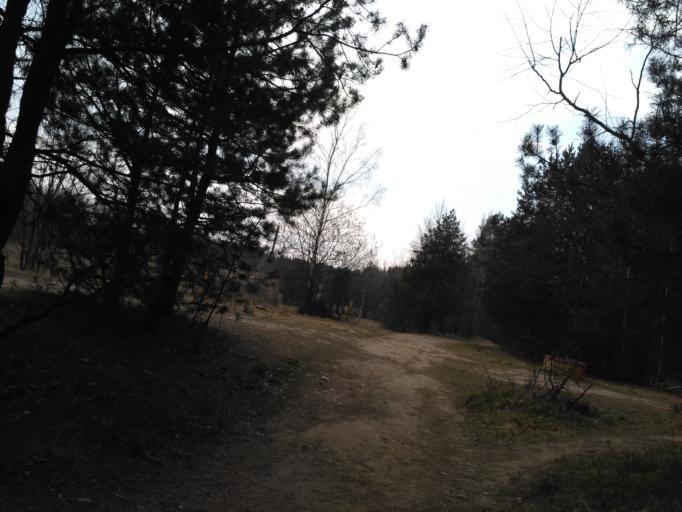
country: BY
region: Minsk
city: Zamostochcha
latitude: 53.8788
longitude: 27.9101
